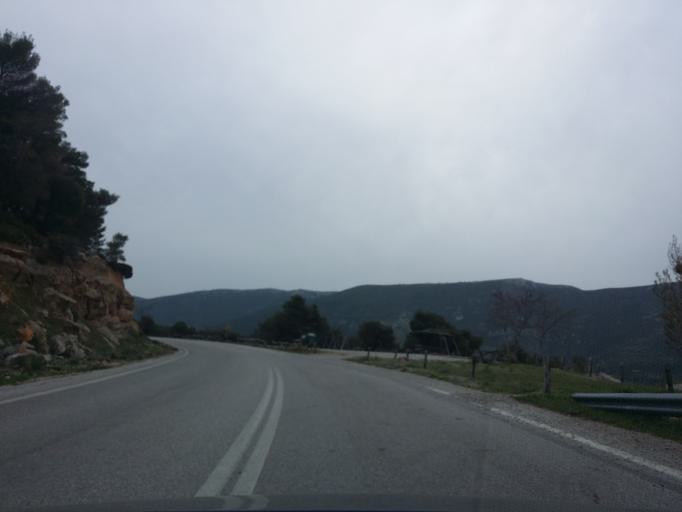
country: GR
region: Central Greece
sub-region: Nomos Voiotias
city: Kaparellion
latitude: 38.1544
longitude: 23.2409
